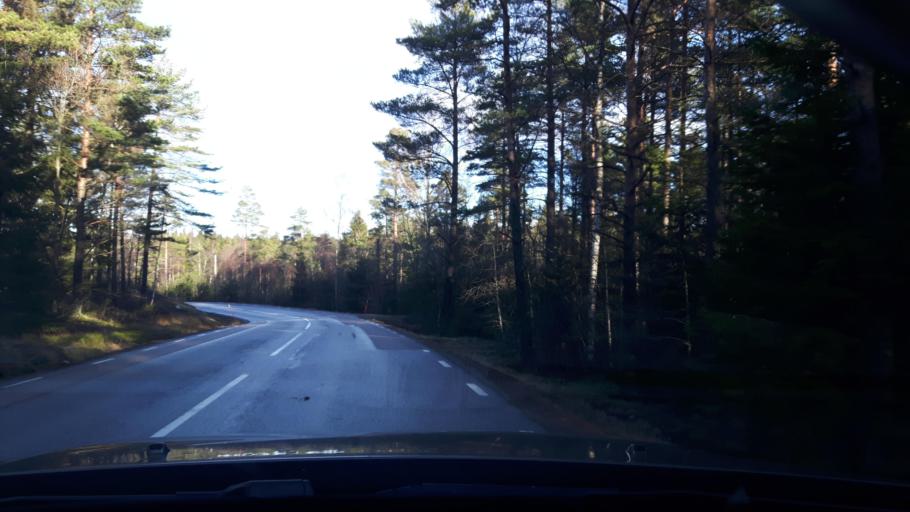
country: SE
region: Vaestra Goetaland
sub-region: Munkedals Kommun
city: Munkedal
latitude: 58.5073
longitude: 11.6818
